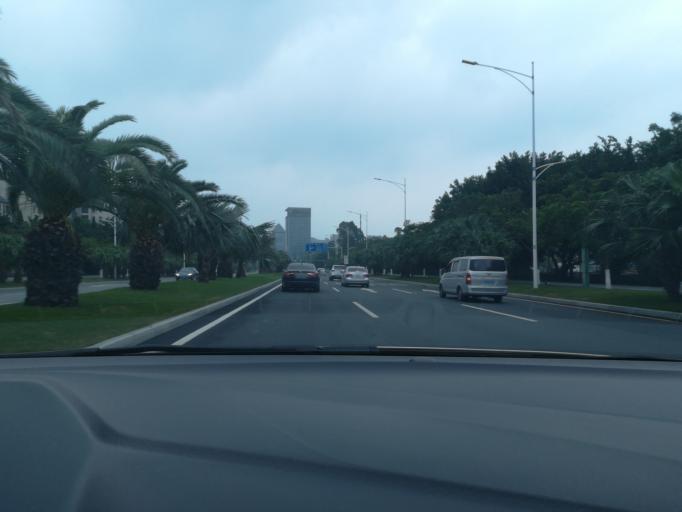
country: CN
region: Guangdong
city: Nansha
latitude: 22.7792
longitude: 113.5954
